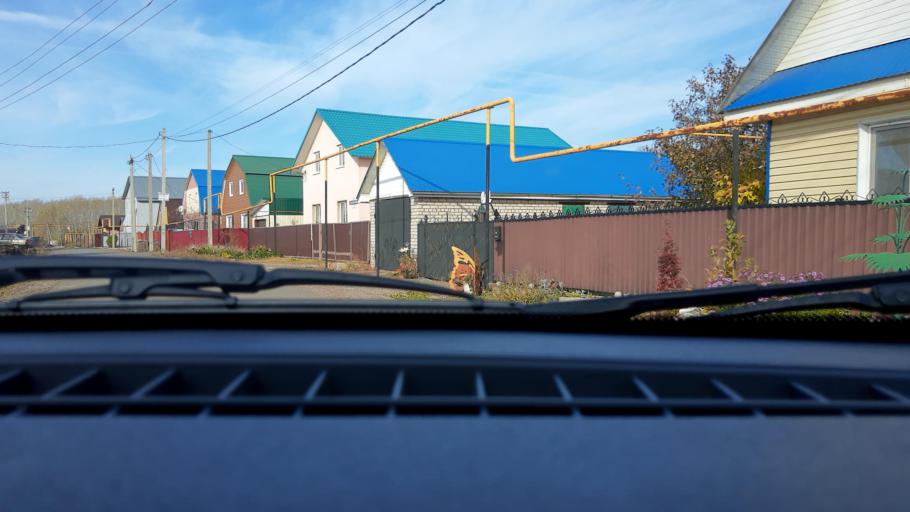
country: RU
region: Bashkortostan
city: Mikhaylovka
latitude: 54.7823
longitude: 55.9063
